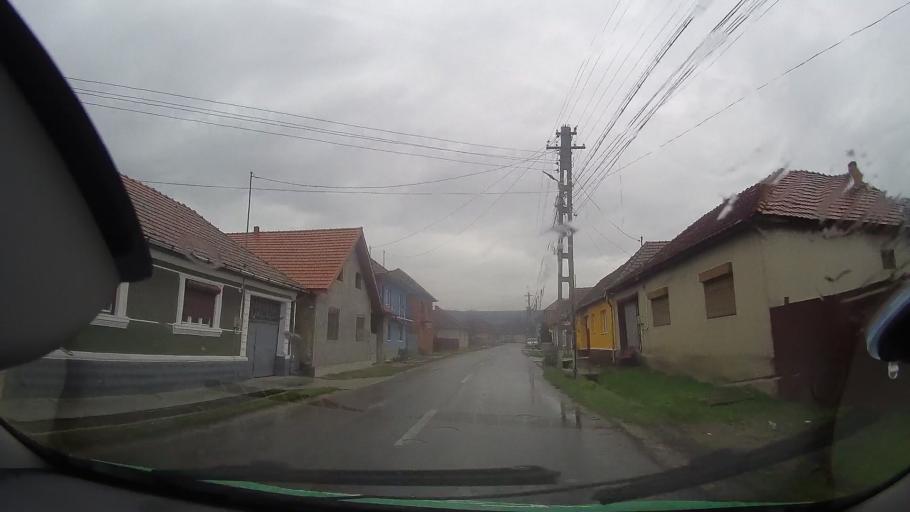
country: RO
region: Bihor
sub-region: Comuna Rabagani
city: Rabagani
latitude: 46.7472
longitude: 22.2339
